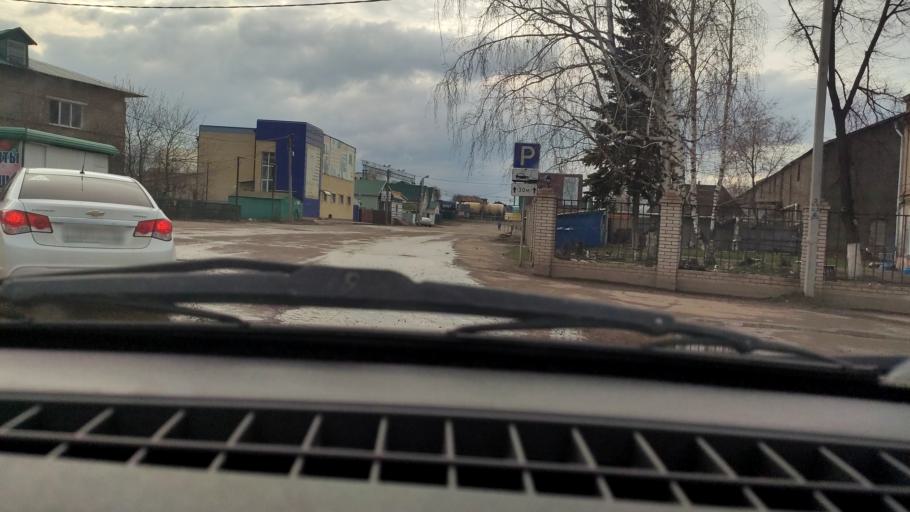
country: RU
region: Bashkortostan
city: Davlekanovo
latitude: 54.2115
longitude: 55.0259
